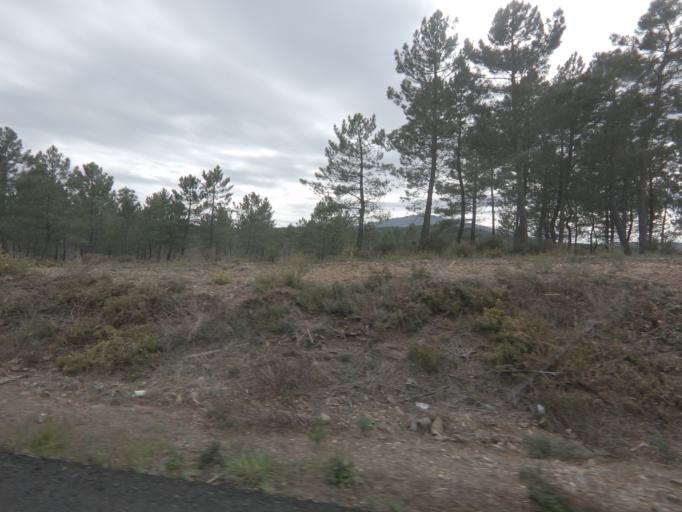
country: ES
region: Extremadura
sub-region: Provincia de Caceres
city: Acebo
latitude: 40.2560
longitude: -6.6891
